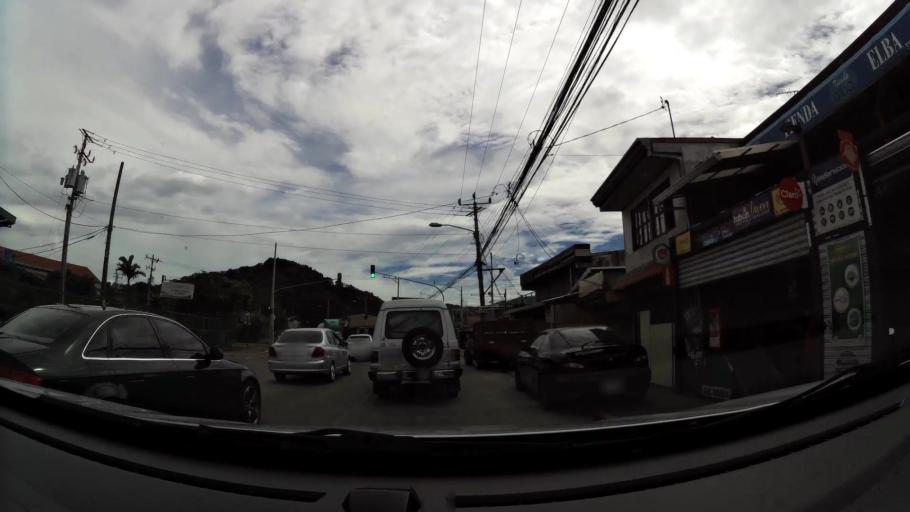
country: CR
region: San Jose
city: Curridabat
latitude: 9.9044
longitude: -84.0486
